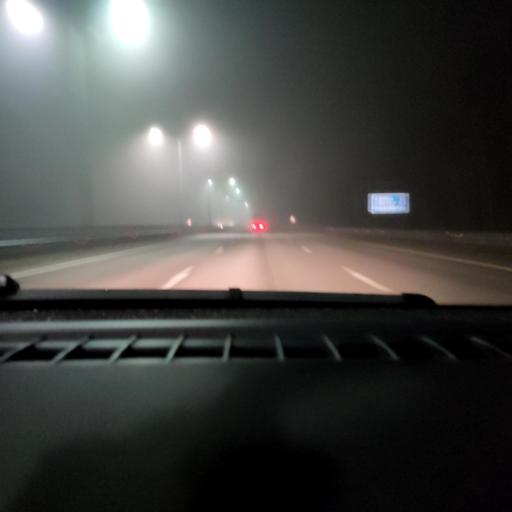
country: RU
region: Voronezj
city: Somovo
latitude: 51.7230
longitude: 39.3104
